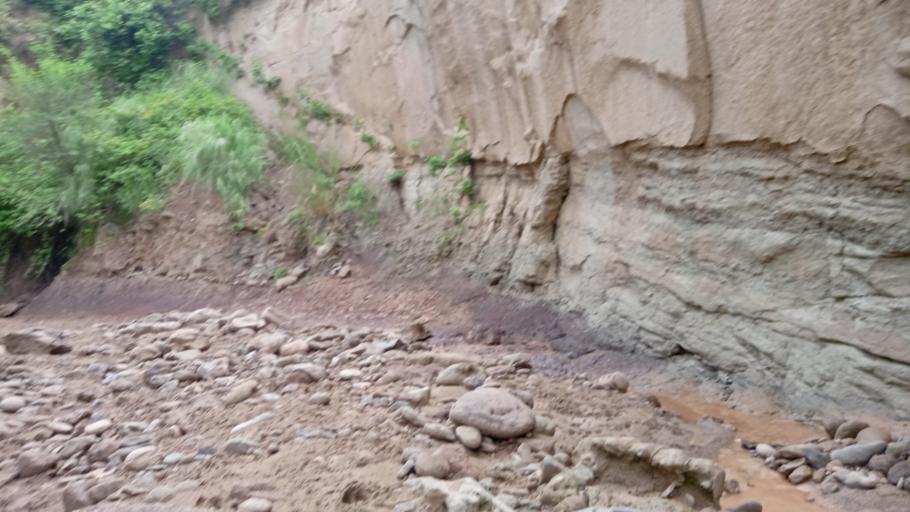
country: IN
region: Haryana
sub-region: Panchkula
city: Pinjaur
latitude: 30.8307
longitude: 76.8409
